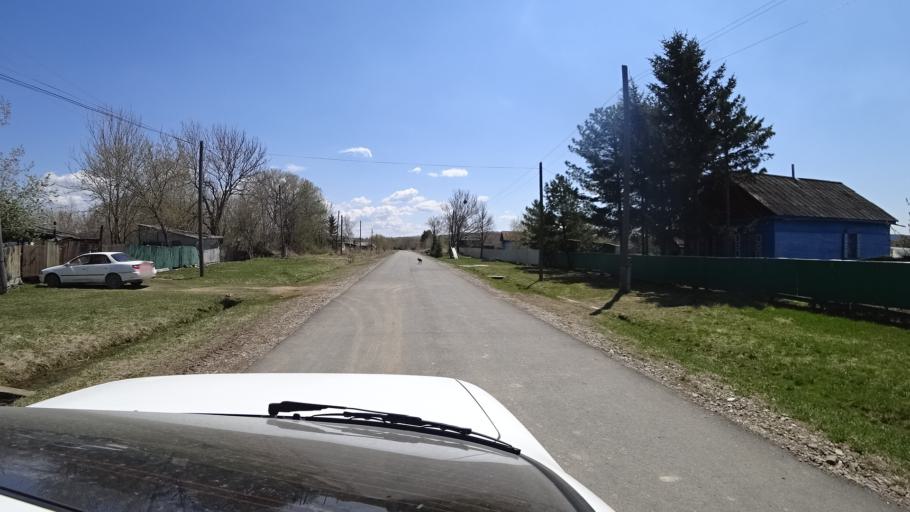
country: RU
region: Primorskiy
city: Dal'nerechensk
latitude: 45.7929
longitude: 133.7694
